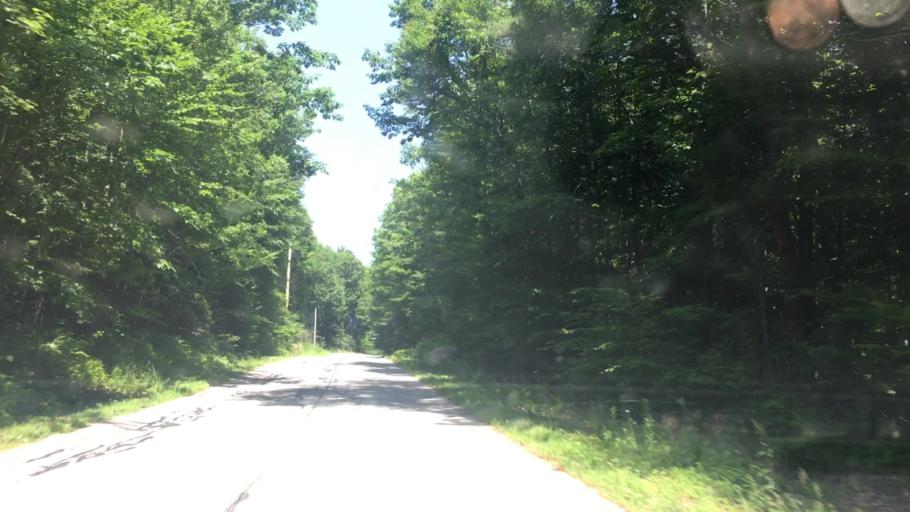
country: US
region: Maine
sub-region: Kennebec County
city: Wayne
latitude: 44.3141
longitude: -70.0570
